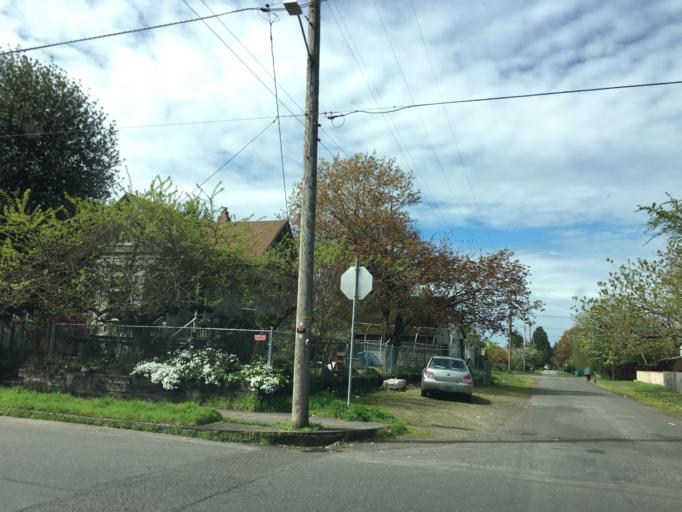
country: US
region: Oregon
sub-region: Multnomah County
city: Lents
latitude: 45.5304
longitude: -122.5866
